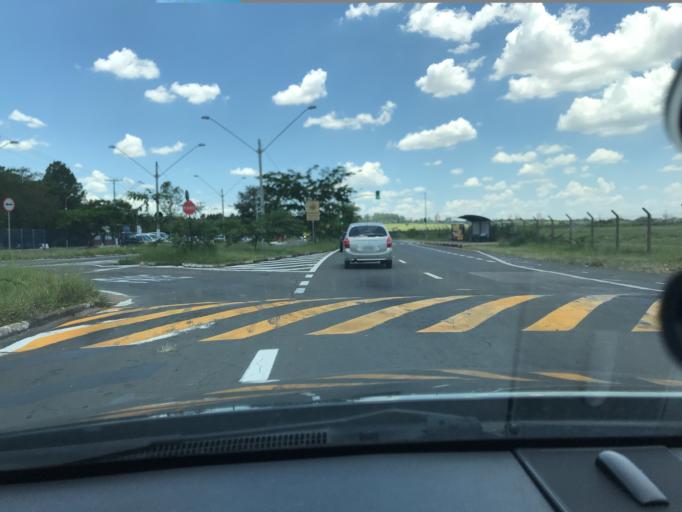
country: BR
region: Sao Paulo
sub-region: Campinas
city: Campinas
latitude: -22.8634
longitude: -47.1029
